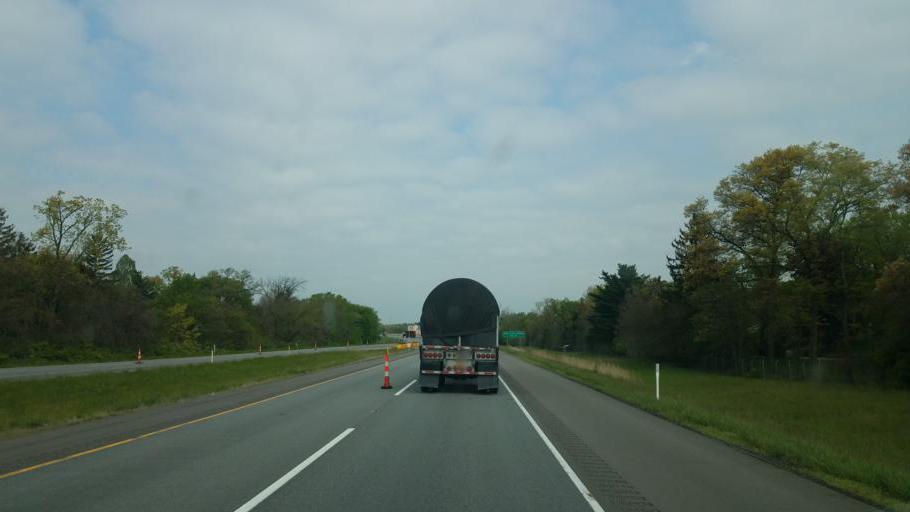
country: US
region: Indiana
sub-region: Saint Joseph County
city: Georgetown
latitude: 41.7191
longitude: -86.2430
